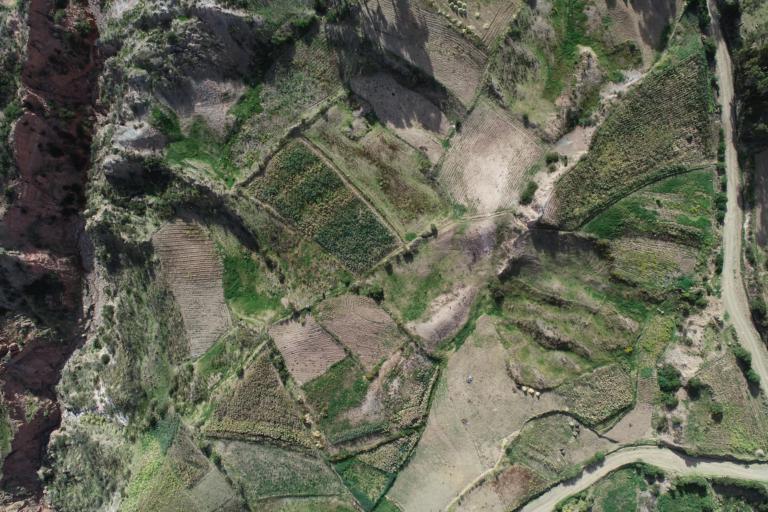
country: BO
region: La Paz
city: La Paz
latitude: -16.5524
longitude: -67.9916
